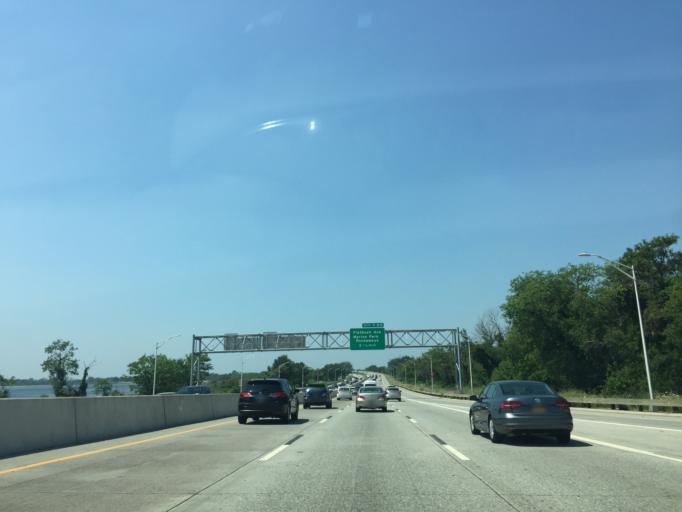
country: US
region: New York
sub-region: Kings County
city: East New York
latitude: 40.6296
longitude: -73.8875
